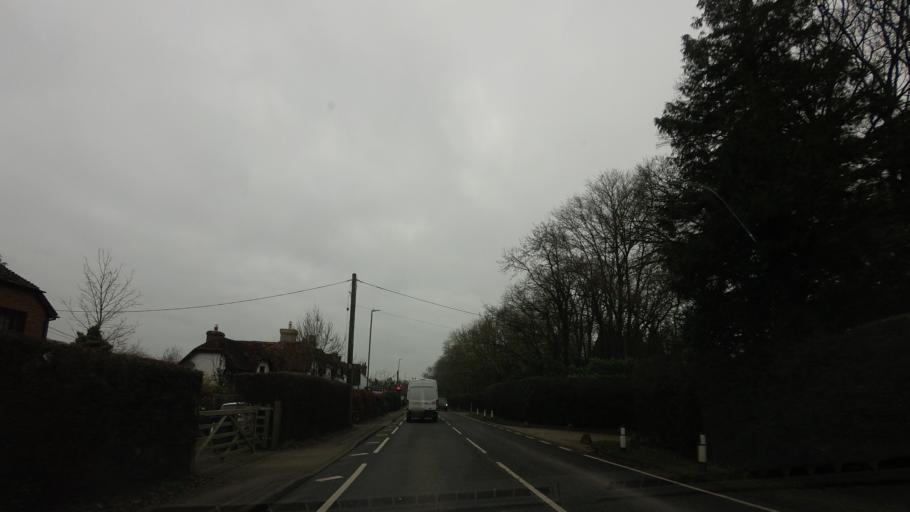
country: GB
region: England
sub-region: Kent
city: Staplehurst
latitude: 51.1520
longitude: 0.5521
